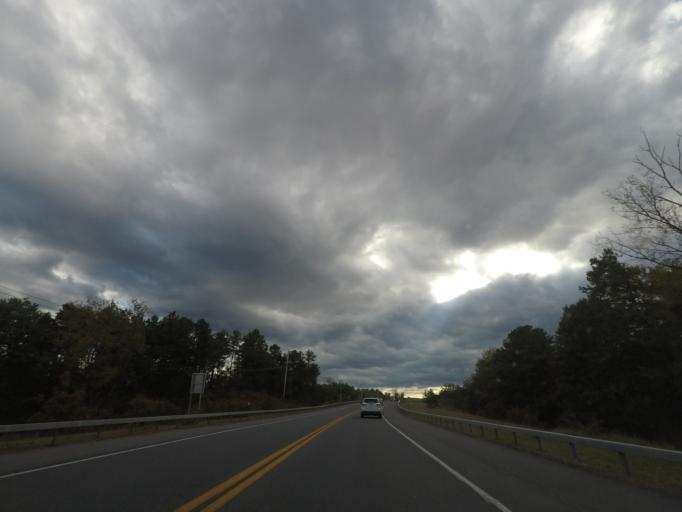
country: US
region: New York
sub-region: Albany County
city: Westmere
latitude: 42.7163
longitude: -73.8674
